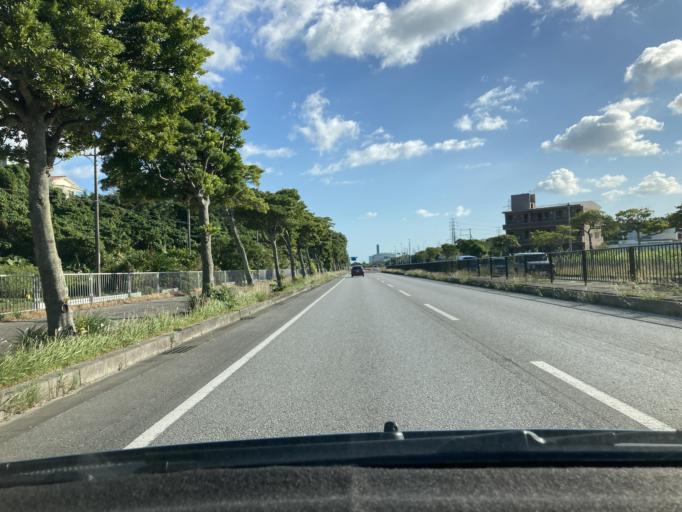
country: JP
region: Okinawa
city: Ishikawa
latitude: 26.4105
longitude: 127.8195
